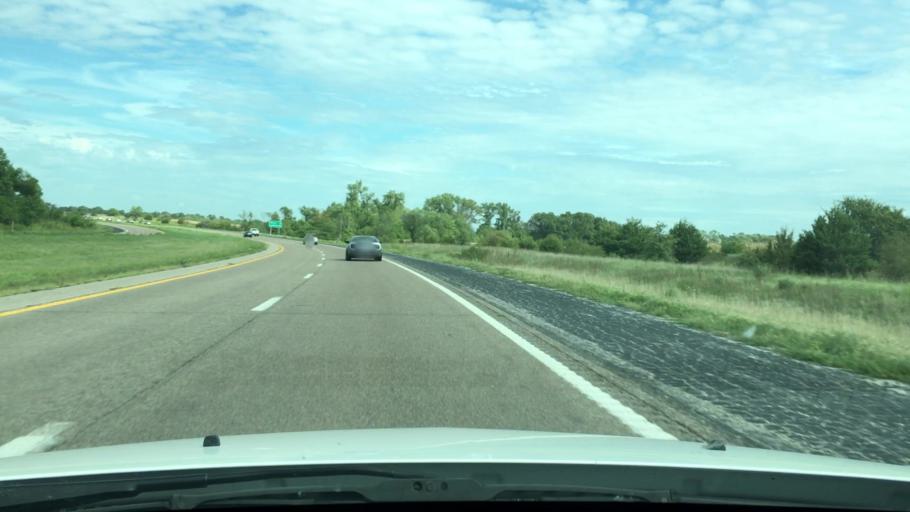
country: US
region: Missouri
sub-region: Audrain County
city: Mexico
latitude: 39.0275
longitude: -91.8855
